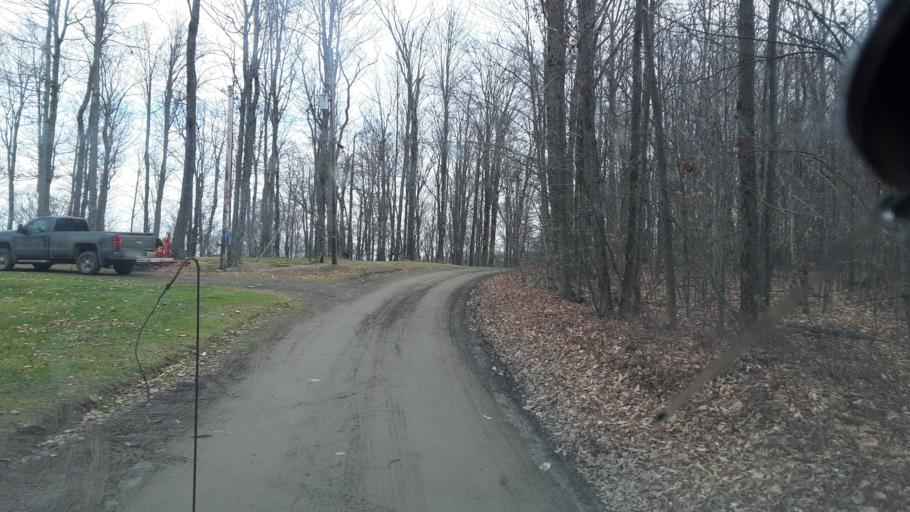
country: US
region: Pennsylvania
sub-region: Tioga County
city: Westfield
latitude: 41.9213
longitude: -77.7018
